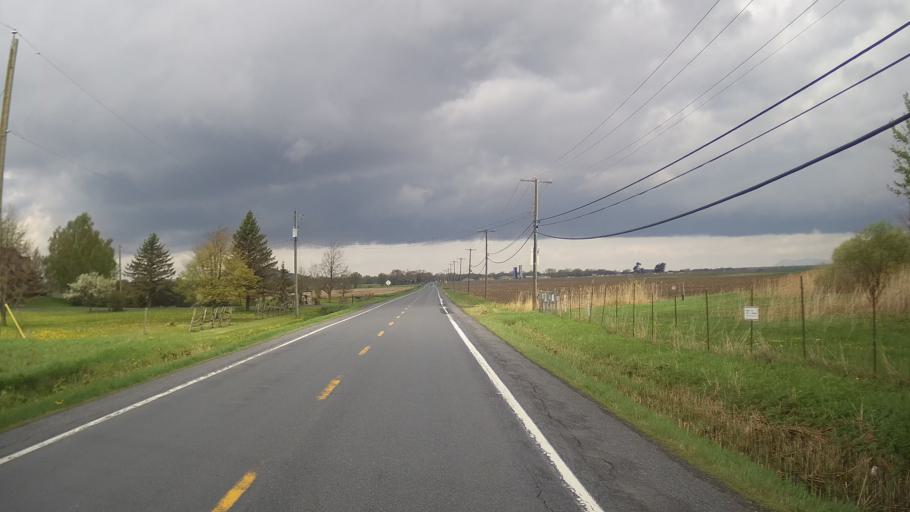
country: CA
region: Quebec
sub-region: Monteregie
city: Farnham
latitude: 45.3108
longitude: -73.0473
